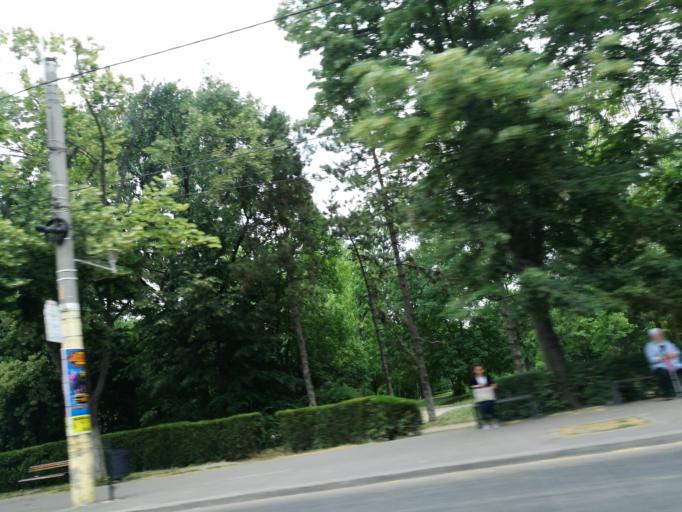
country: RO
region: Constanta
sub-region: Municipiul Constanta
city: Constanta
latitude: 44.2087
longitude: 28.6290
